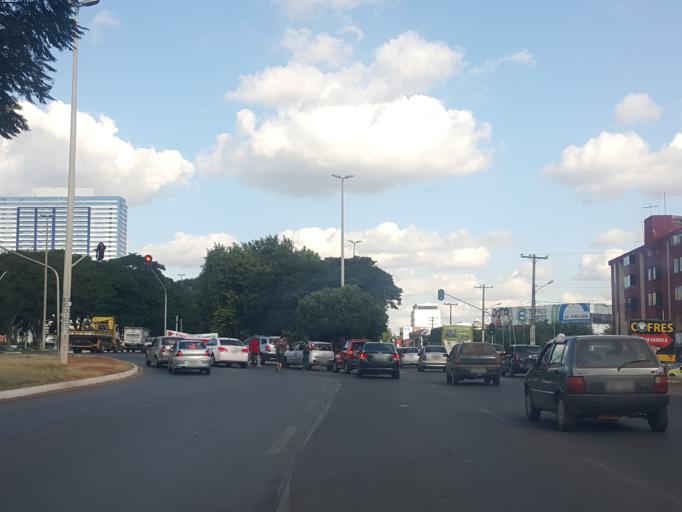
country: BR
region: Federal District
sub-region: Brasilia
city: Brasilia
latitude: -15.8365
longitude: -48.0490
